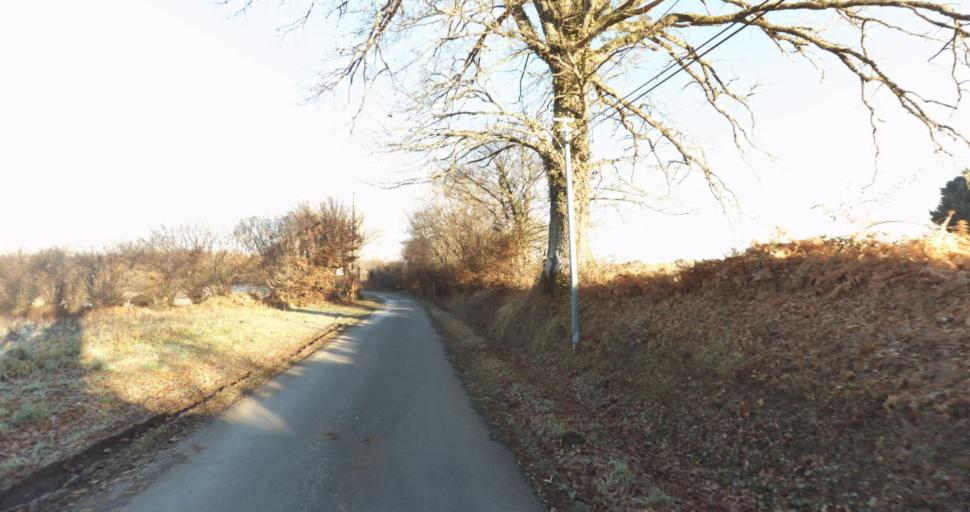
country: FR
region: Limousin
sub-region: Departement de la Haute-Vienne
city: Aixe-sur-Vienne
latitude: 45.8165
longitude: 1.1423
